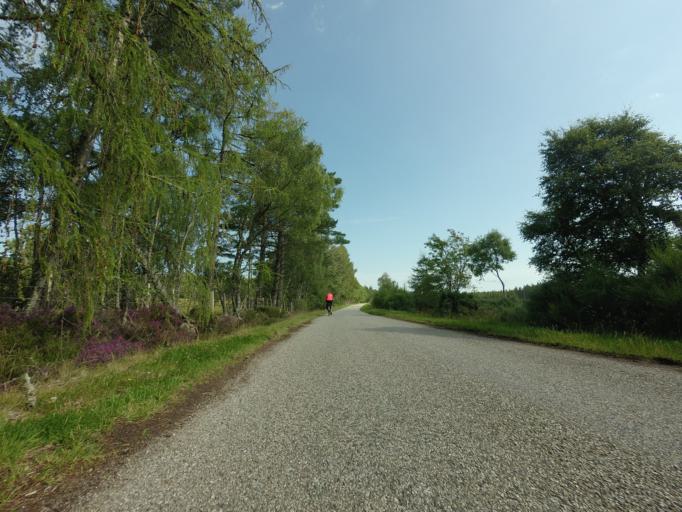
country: GB
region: Scotland
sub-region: Highland
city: Invergordon
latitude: 57.7351
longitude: -4.1901
